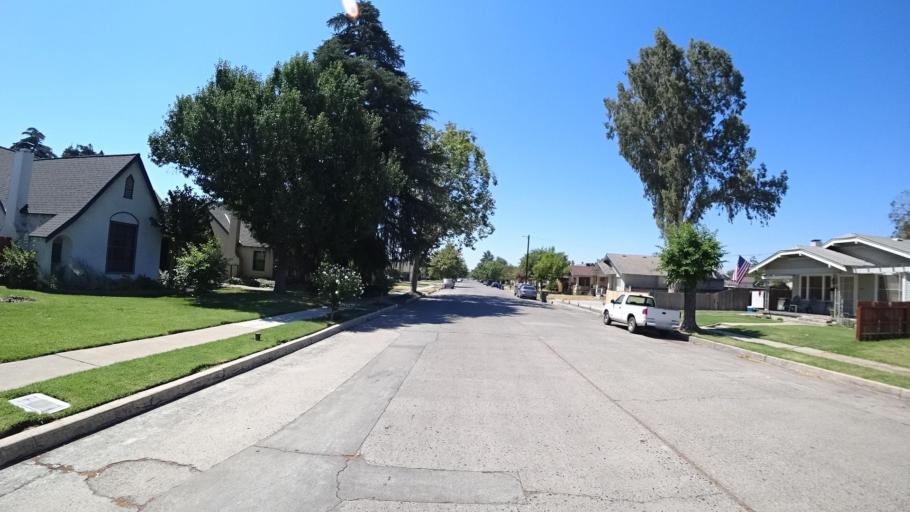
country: US
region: California
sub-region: Fresno County
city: Fresno
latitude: 36.7623
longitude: -119.8057
